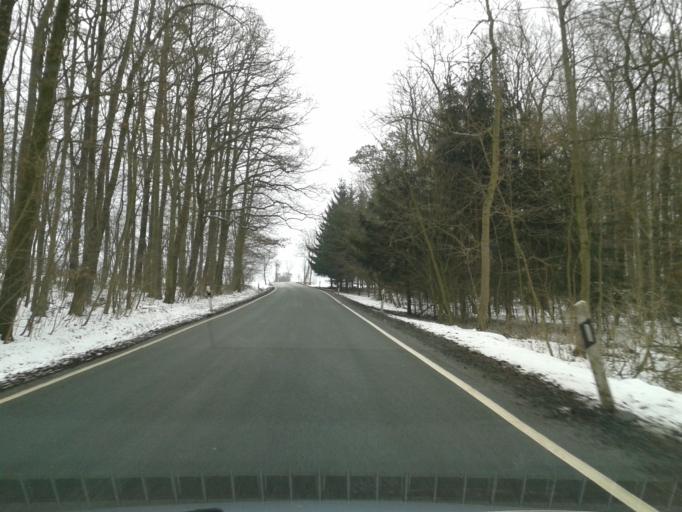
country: DE
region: Thuringia
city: Lehesten
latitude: 50.9601
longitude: 11.5437
